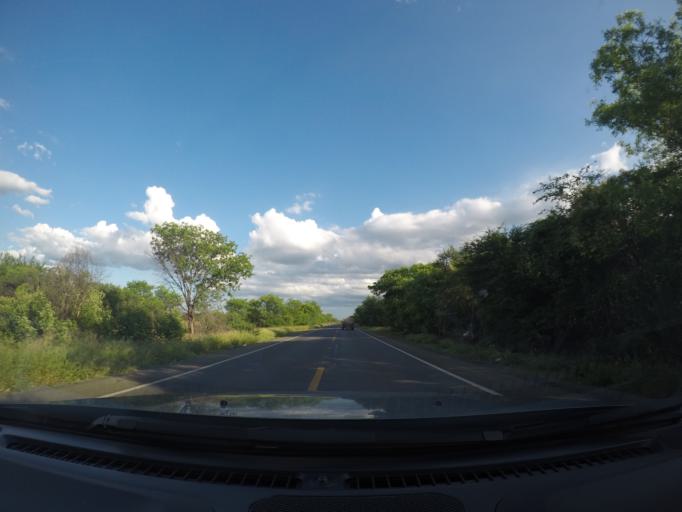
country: BR
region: Bahia
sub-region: Oliveira Dos Brejinhos
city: Beira Rio
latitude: -12.2253
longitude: -42.7868
